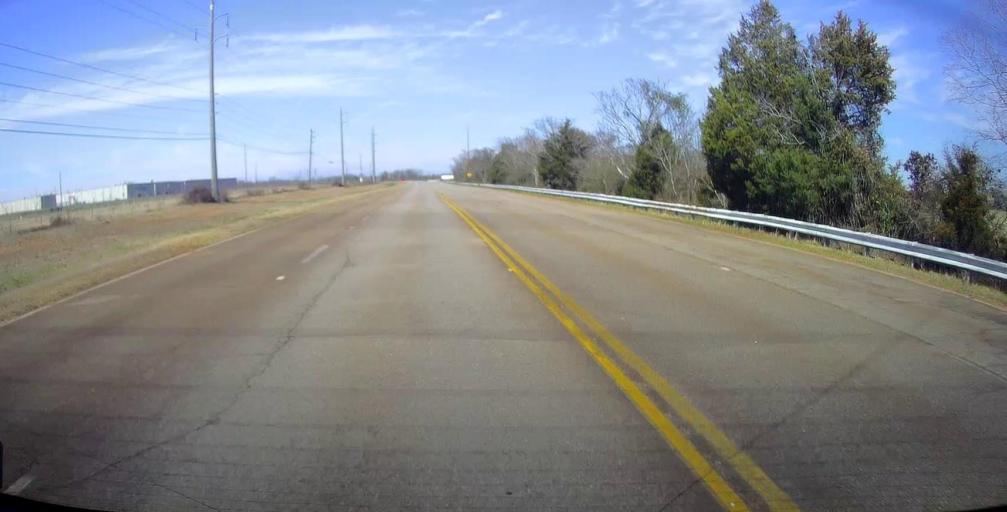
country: US
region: Georgia
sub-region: Houston County
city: Perry
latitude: 32.4868
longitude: -83.7588
